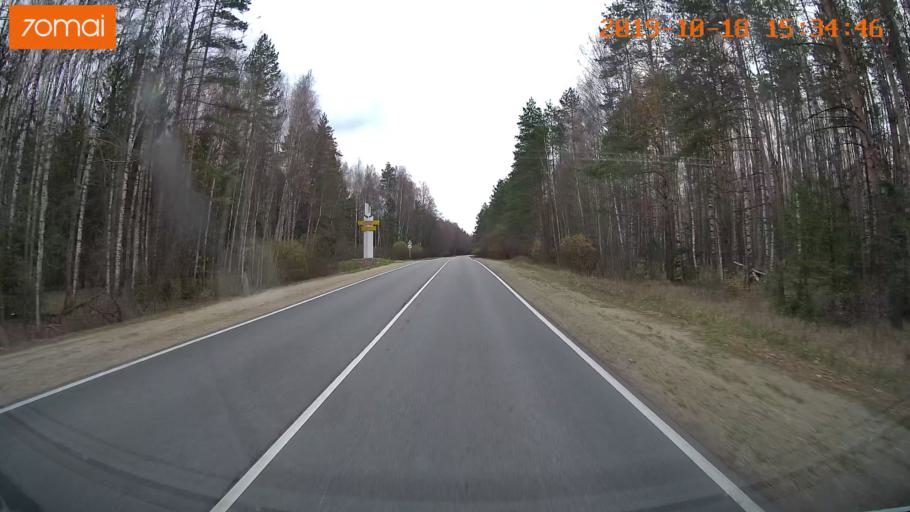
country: RU
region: Vladimir
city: Anopino
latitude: 55.8584
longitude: 40.6382
